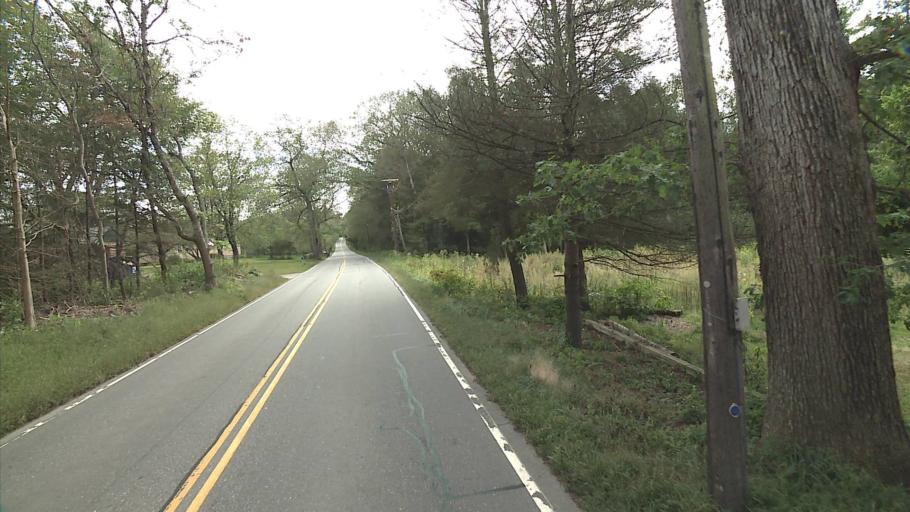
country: US
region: Connecticut
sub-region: New London County
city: Jewett City
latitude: 41.6411
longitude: -71.9571
